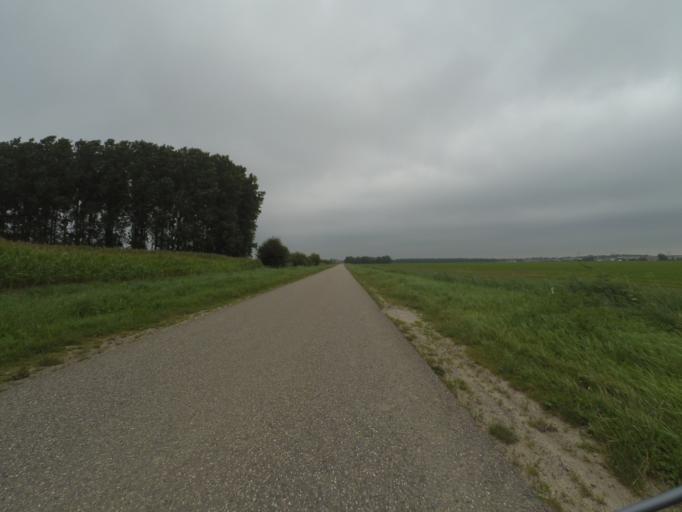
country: NL
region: Flevoland
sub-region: Gemeente Lelystad
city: Lelystad
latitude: 52.4837
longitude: 5.4737
